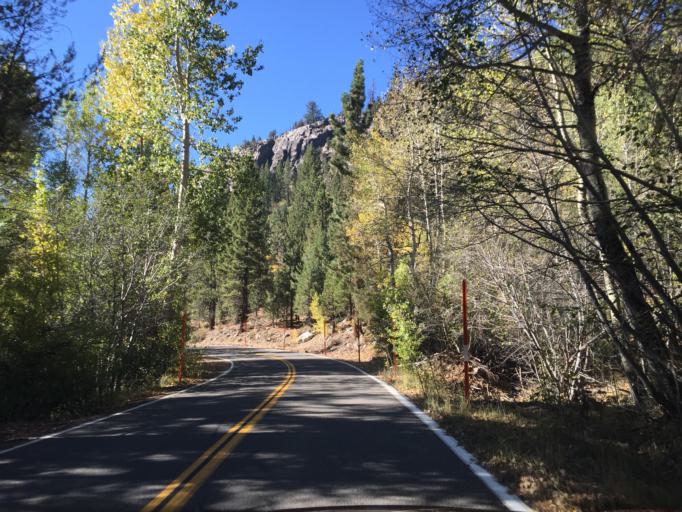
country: US
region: California
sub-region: Mono County
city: Bridgeport
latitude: 38.3332
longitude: -119.5536
